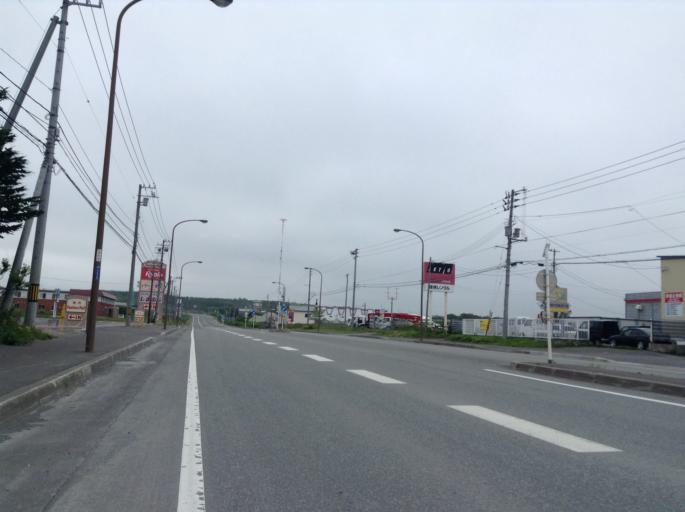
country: JP
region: Hokkaido
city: Wakkanai
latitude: 45.3810
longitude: 141.7094
